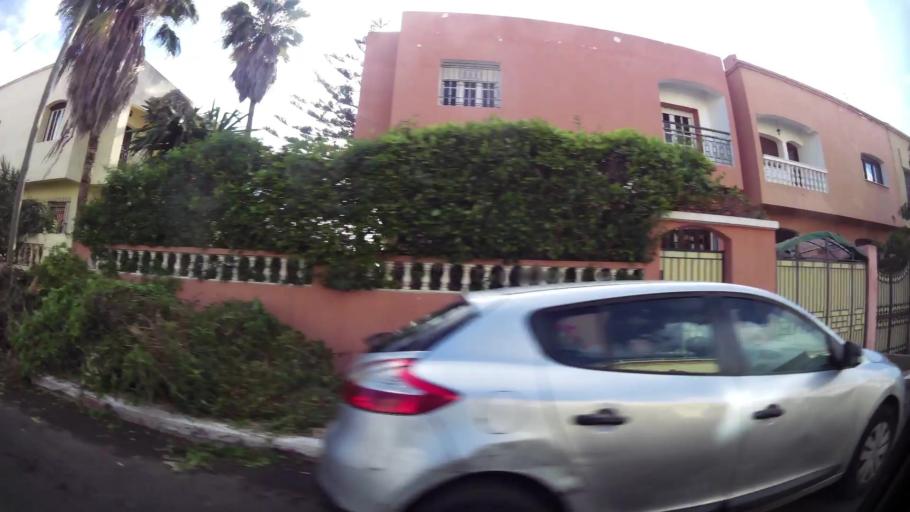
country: MA
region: Grand Casablanca
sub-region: Casablanca
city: Casablanca
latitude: 33.5734
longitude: -7.6884
